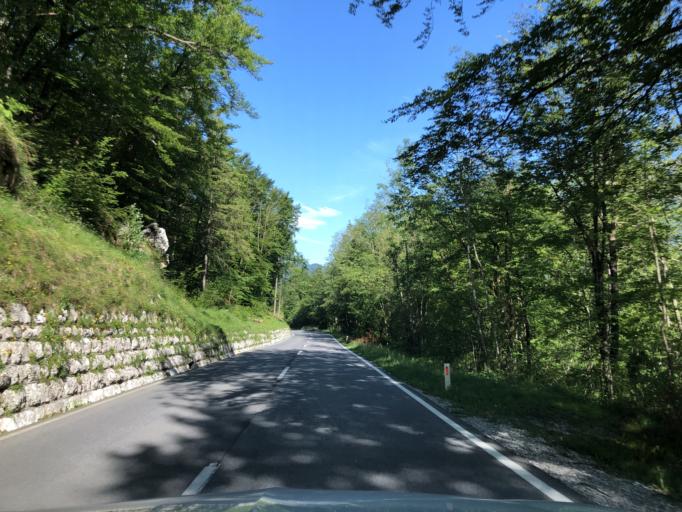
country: SI
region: Kobarid
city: Kobarid
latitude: 46.2753
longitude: 13.5672
